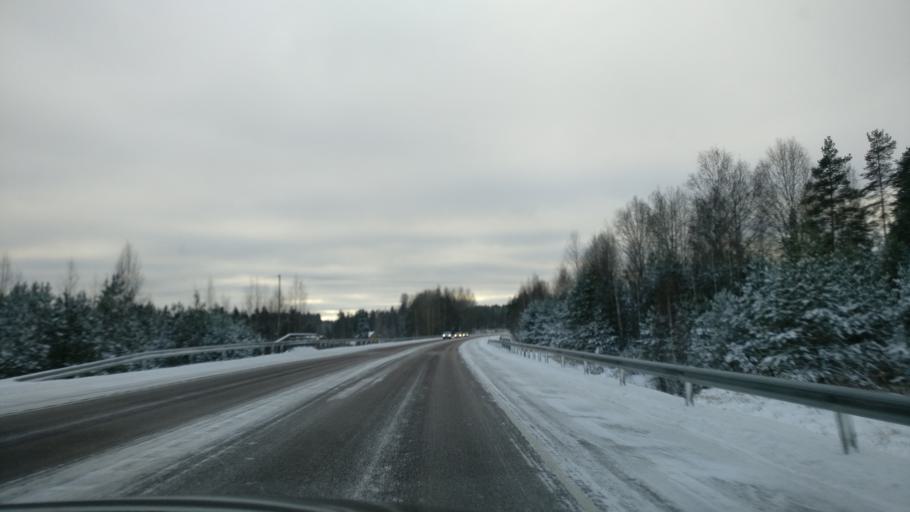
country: FI
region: Paijanne Tavastia
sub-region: Lahti
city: Heinola
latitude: 61.3245
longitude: 26.1556
